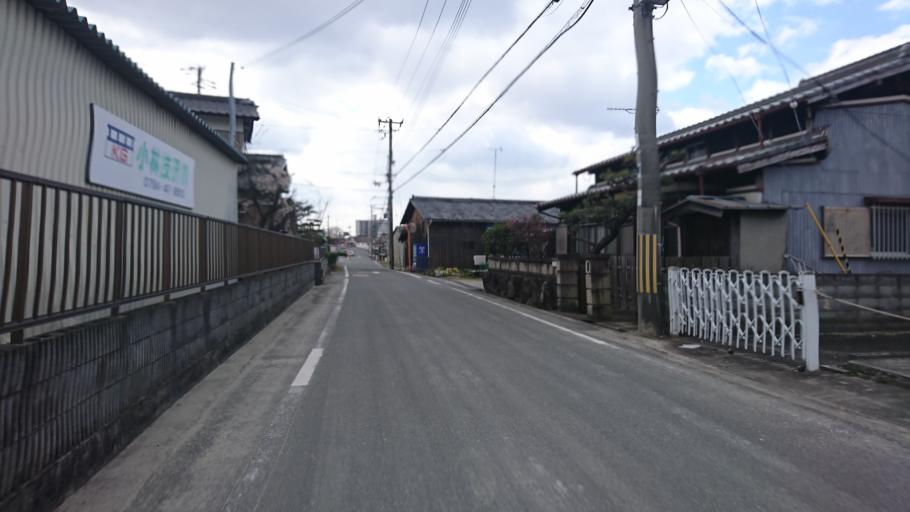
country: JP
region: Hyogo
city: Kakogawacho-honmachi
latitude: 34.7971
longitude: 134.8079
